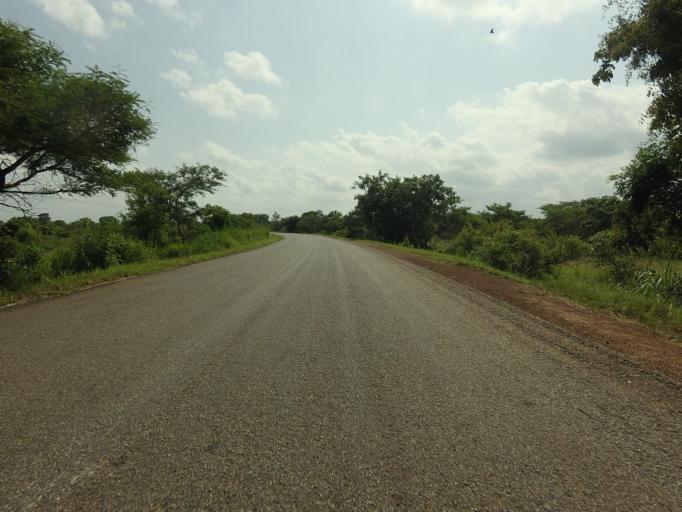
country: GH
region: Volta
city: Ho
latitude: 6.3941
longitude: 0.8092
